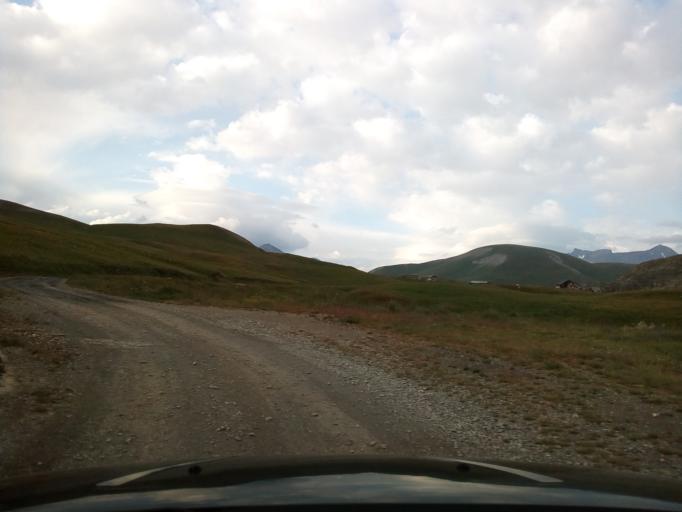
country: FR
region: Rhone-Alpes
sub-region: Departement de l'Isere
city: Mont-de-Lans
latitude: 45.0524
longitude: 6.2077
